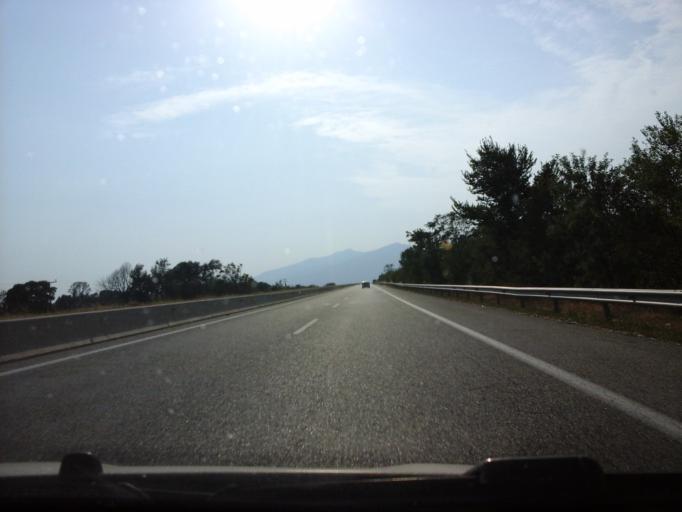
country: GR
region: East Macedonia and Thrace
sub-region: Nomos Xanthis
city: Selero
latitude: 41.1170
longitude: 25.0085
